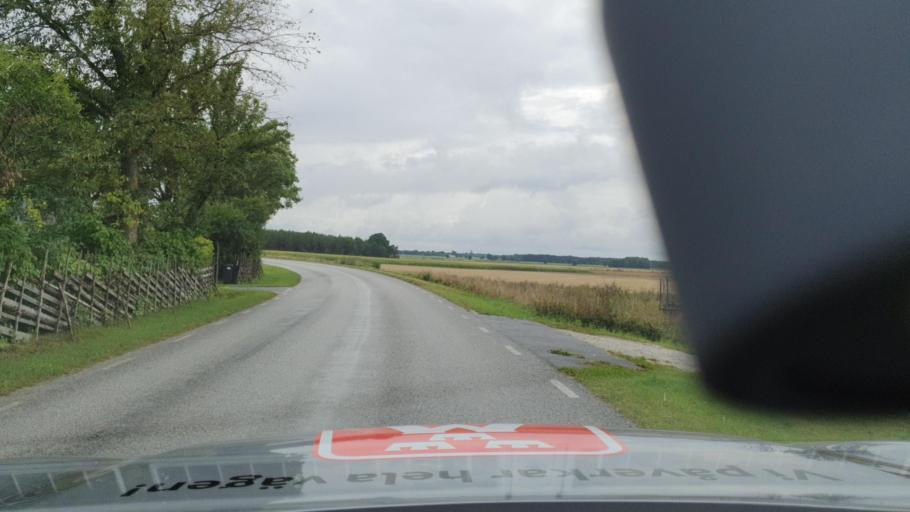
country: SE
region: Gotland
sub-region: Gotland
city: Slite
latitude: 57.5759
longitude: 18.6030
